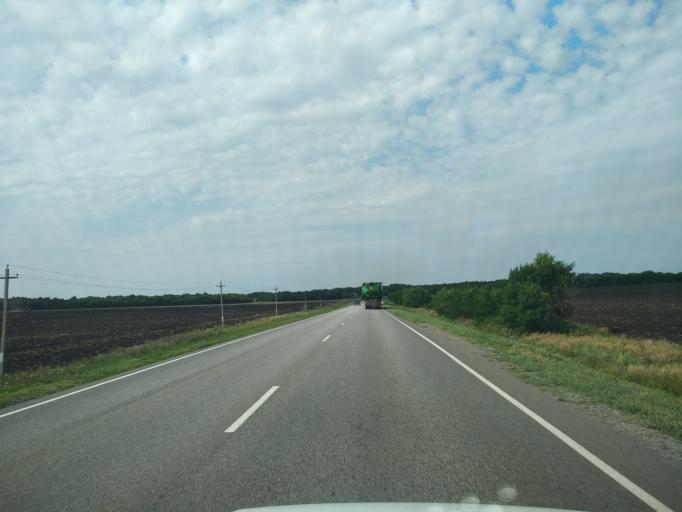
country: RU
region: Voronezj
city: Pereleshinskiy
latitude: 51.8825
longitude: 40.4226
